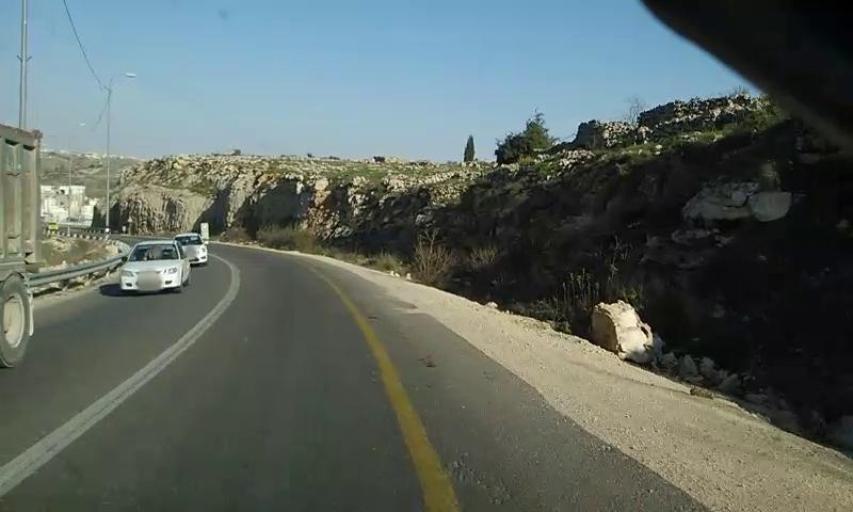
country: PS
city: Khallat ad Dar
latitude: 31.5006
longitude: 35.1133
